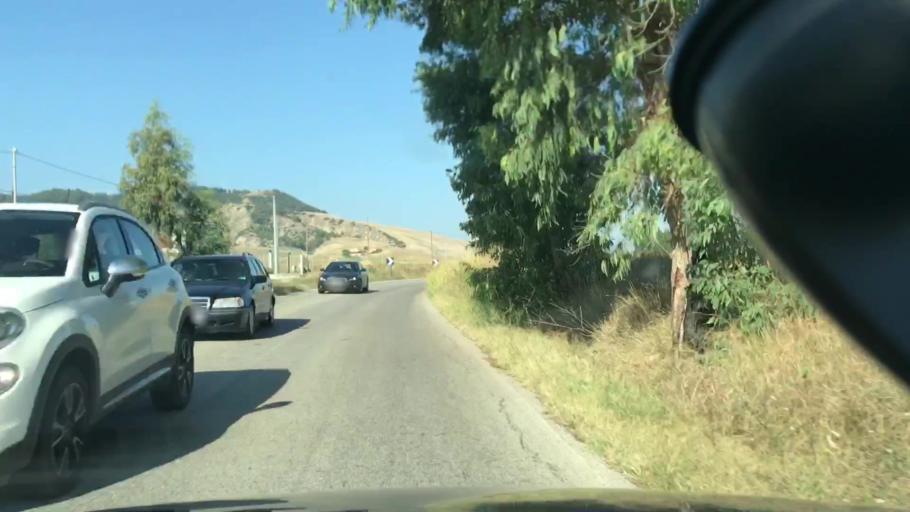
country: IT
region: Basilicate
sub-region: Provincia di Matera
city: La Martella
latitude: 40.6585
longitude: 16.5178
